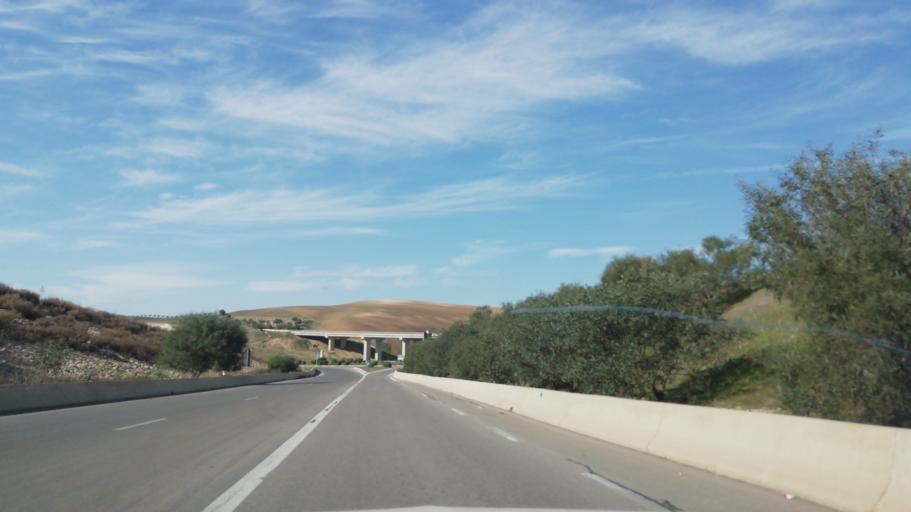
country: DZ
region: Tlemcen
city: Chetouane
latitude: 34.9800
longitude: -1.2357
